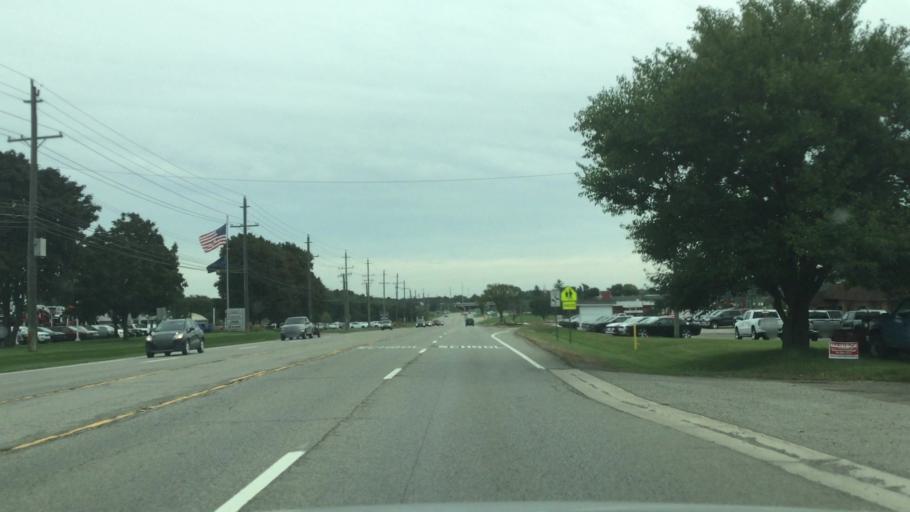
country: US
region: Michigan
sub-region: Oakland County
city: Clarkston
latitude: 42.7446
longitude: -83.4626
